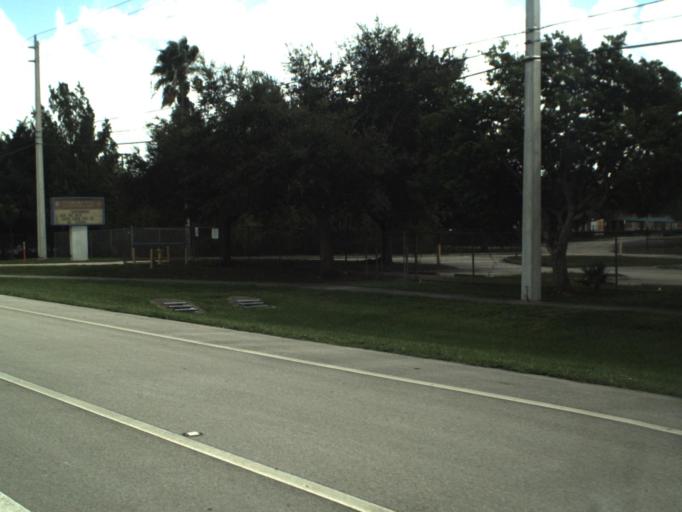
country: US
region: Florida
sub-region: Broward County
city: Sunshine Ranches
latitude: 26.0272
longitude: -80.3123
